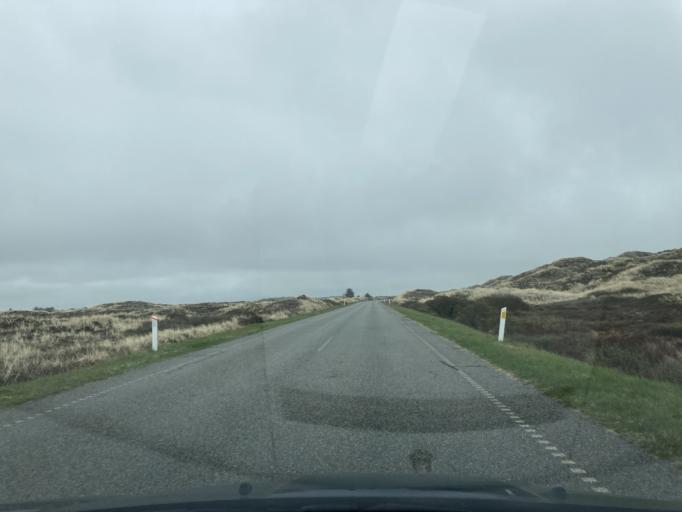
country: DK
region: North Denmark
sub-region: Thisted Kommune
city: Hurup
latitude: 56.9276
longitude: 8.3497
